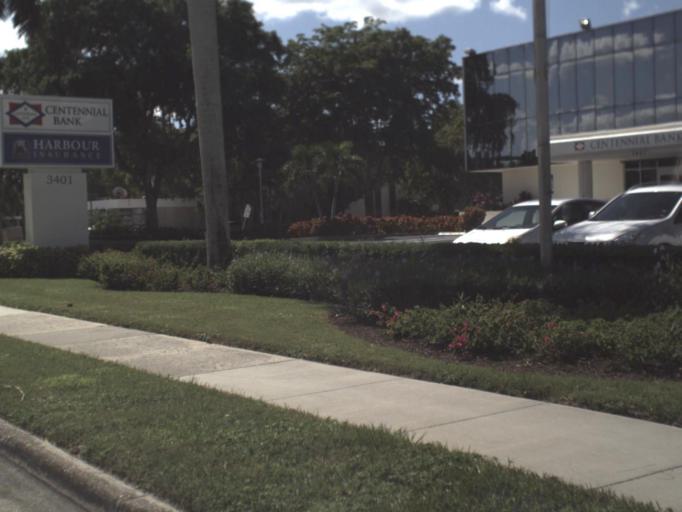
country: US
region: Florida
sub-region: Collier County
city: Pine Ridge
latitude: 26.1892
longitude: -81.8001
